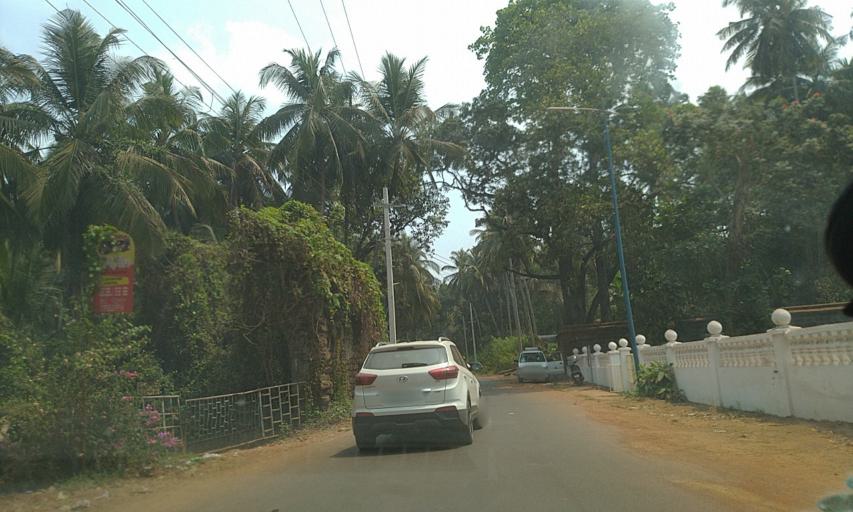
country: IN
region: Goa
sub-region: North Goa
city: Jua
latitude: 15.5037
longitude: 73.9101
